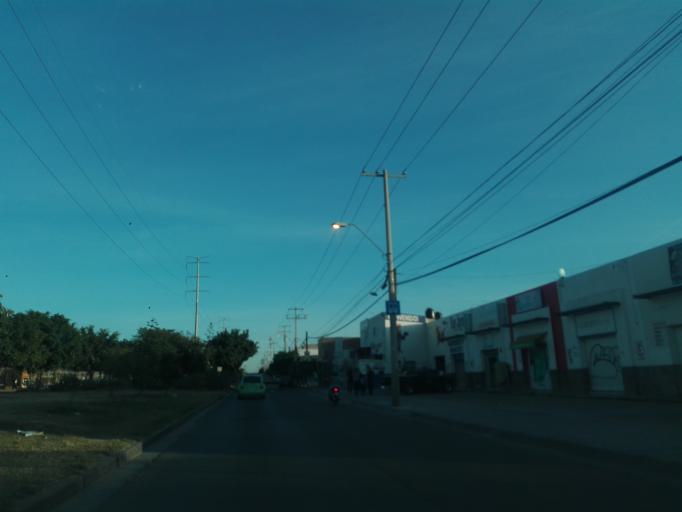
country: MX
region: Guanajuato
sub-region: Leon
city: Fraccionamiento Paraiso Real
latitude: 21.0812
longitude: -101.6238
